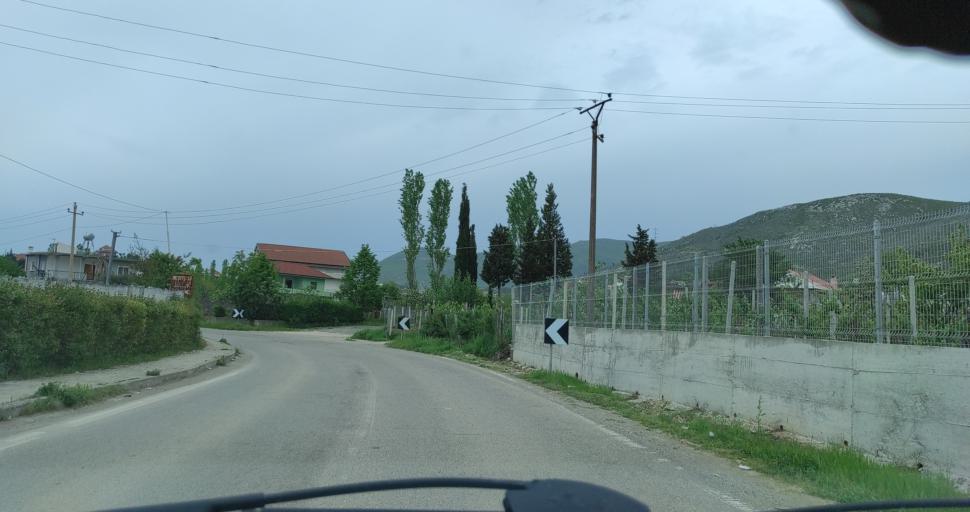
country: AL
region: Lezhe
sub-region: Rrethi i Kurbinit
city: Lac
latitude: 41.6178
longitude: 19.7116
